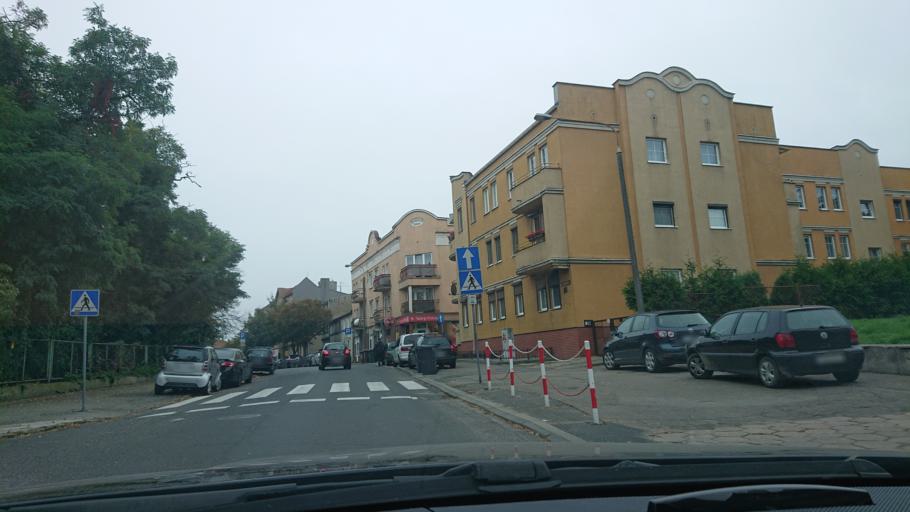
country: PL
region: Greater Poland Voivodeship
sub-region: Powiat gnieznienski
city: Gniezno
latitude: 52.5404
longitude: 17.5998
